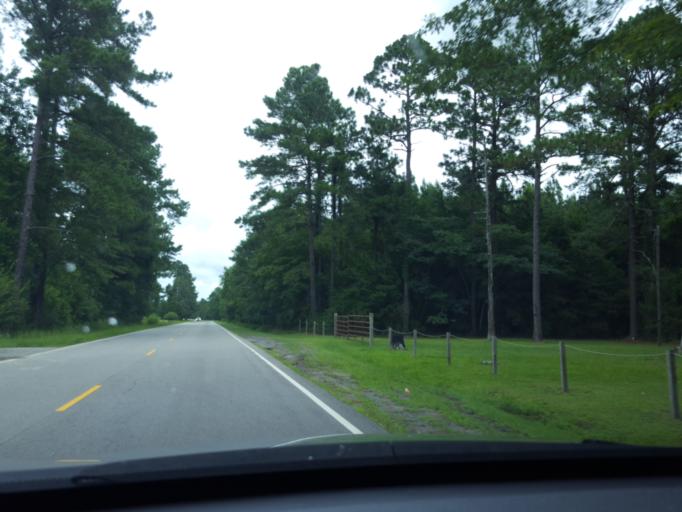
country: US
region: North Carolina
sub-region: Beaufort County
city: Washington
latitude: 35.6783
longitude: -76.9970
